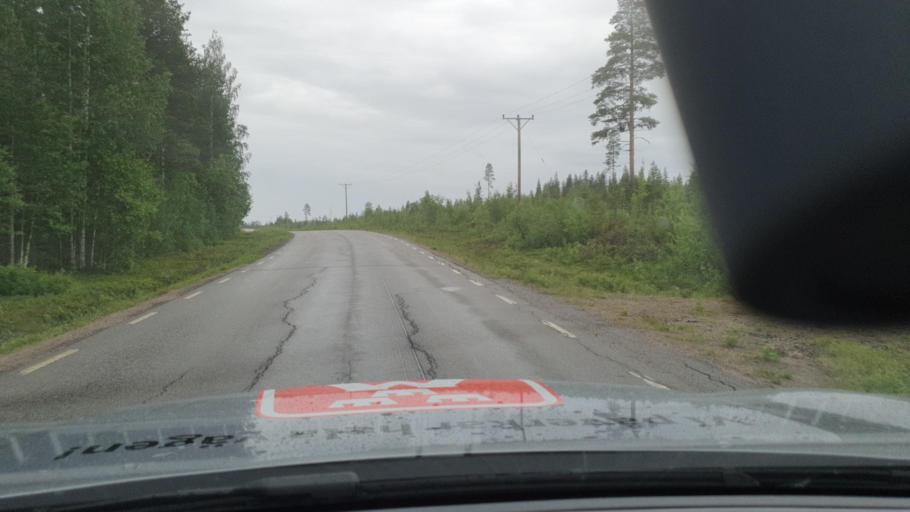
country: SE
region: Norrbotten
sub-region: Pajala Kommun
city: Pajala
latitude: 66.7889
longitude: 23.1272
